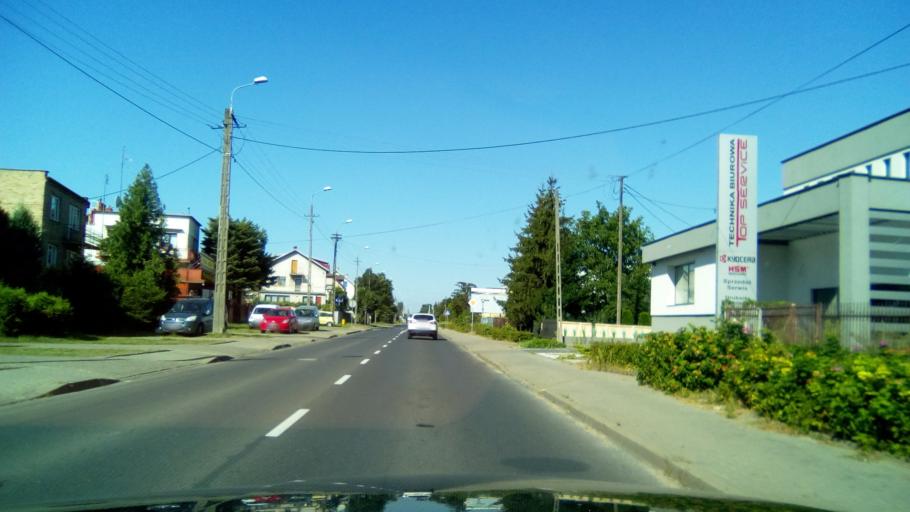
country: PL
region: Masovian Voivodeship
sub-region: Plock
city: Plock
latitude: 52.5390
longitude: 19.7289
